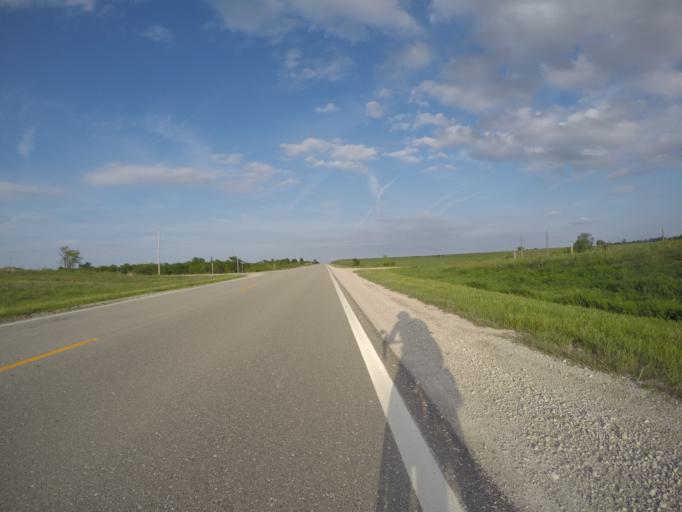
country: US
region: Kansas
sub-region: Pottawatomie County
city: Westmoreland
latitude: 39.4283
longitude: -96.5881
